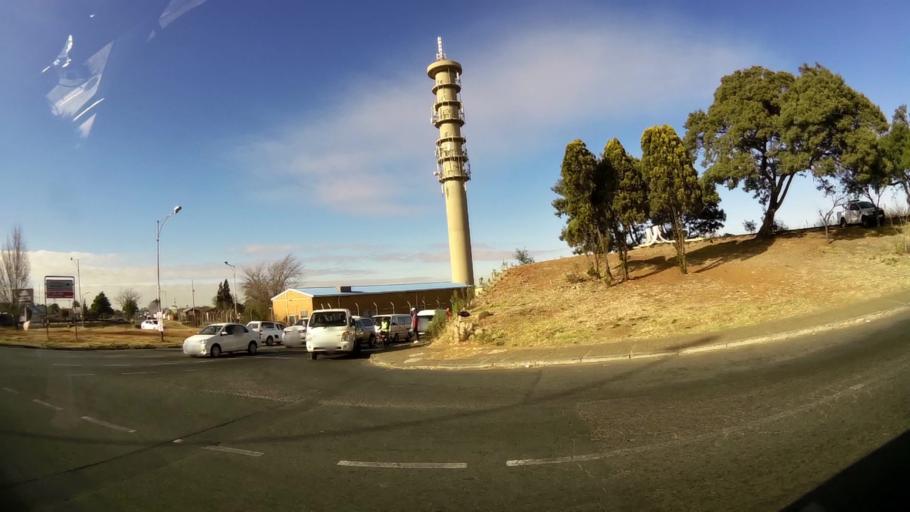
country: ZA
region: Gauteng
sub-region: West Rand District Municipality
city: Krugersdorp
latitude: -26.1199
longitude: 27.8175
